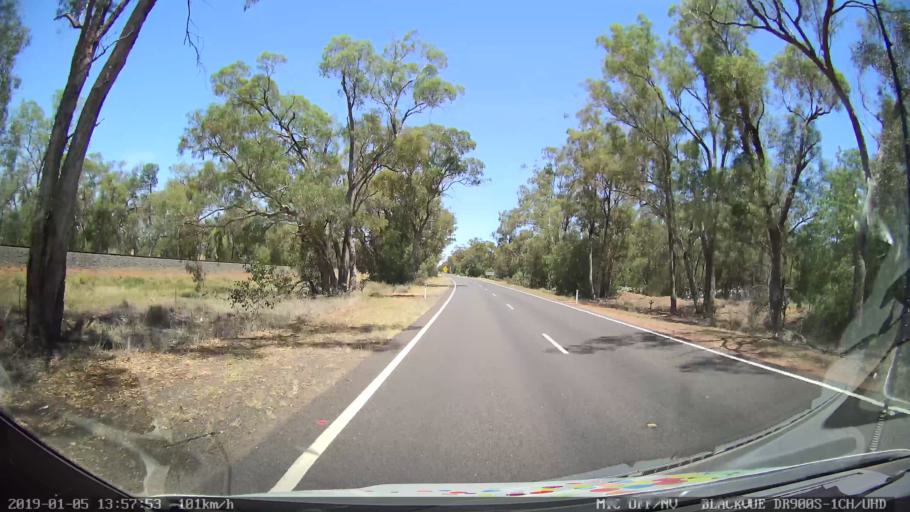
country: AU
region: New South Wales
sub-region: Gunnedah
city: Gunnedah
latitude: -31.1329
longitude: 150.2780
